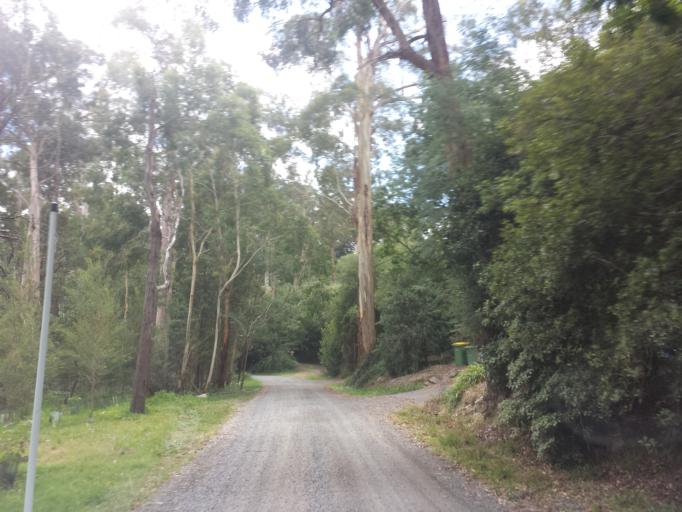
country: AU
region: Victoria
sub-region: Yarra Ranges
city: Belgrave Heights
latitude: -37.9204
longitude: 145.3576
